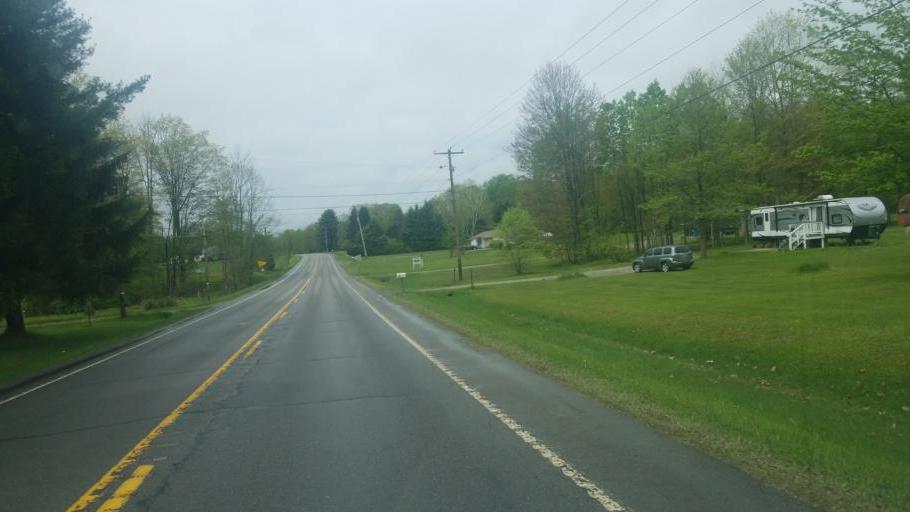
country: US
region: Pennsylvania
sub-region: Forest County
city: Marienville
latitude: 41.4504
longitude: -79.1679
